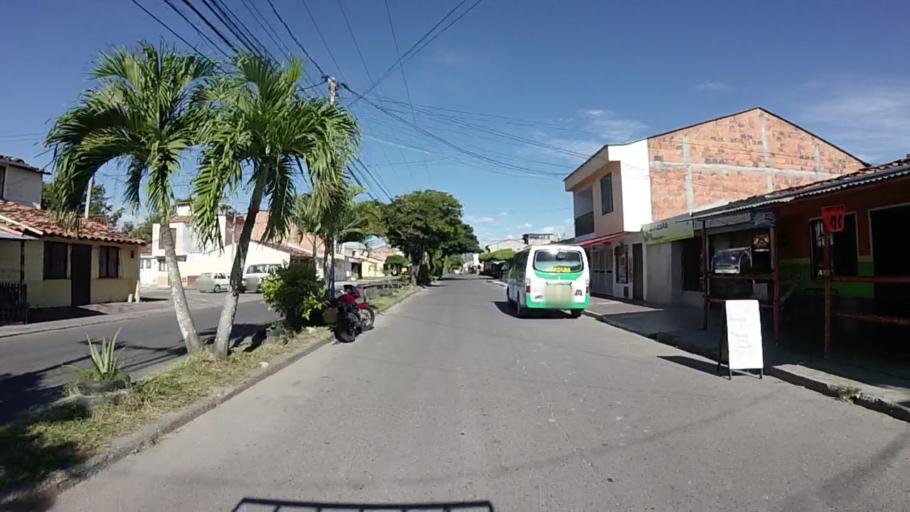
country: CO
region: Valle del Cauca
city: Cartago
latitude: 4.7592
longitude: -75.9235
